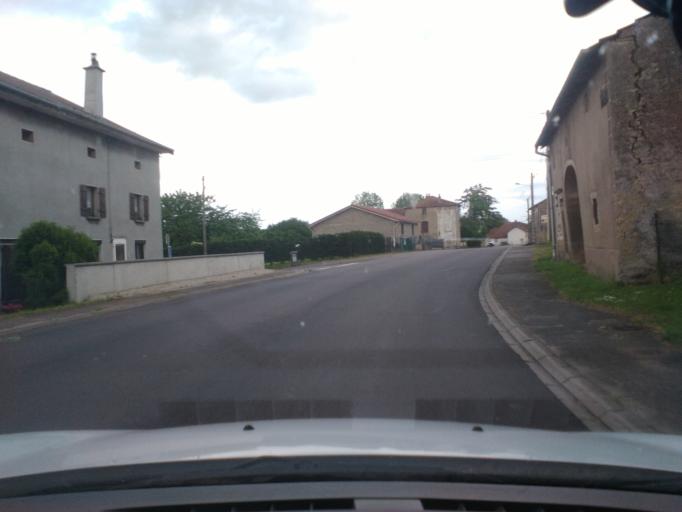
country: FR
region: Lorraine
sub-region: Departement des Vosges
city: Mirecourt
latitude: 48.3107
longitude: 6.0980
